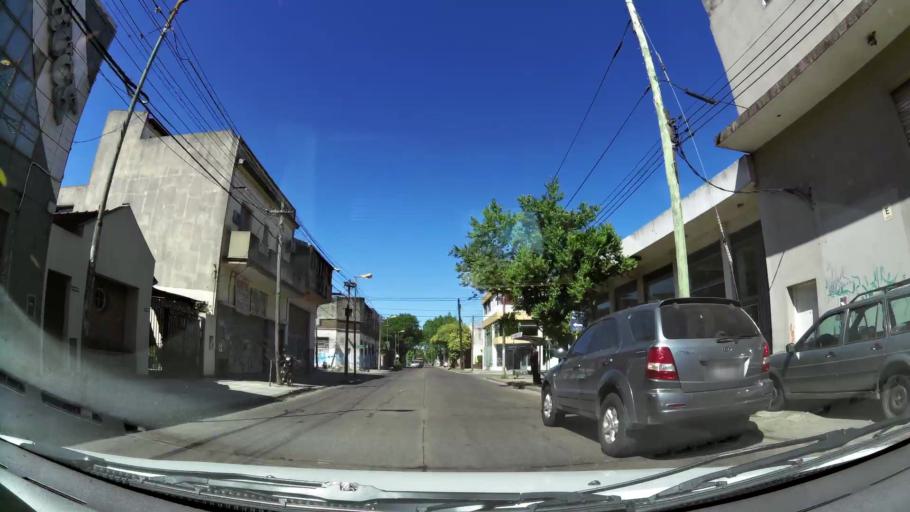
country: AR
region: Buenos Aires
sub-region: Partido de General San Martin
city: General San Martin
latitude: -34.5617
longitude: -58.5281
